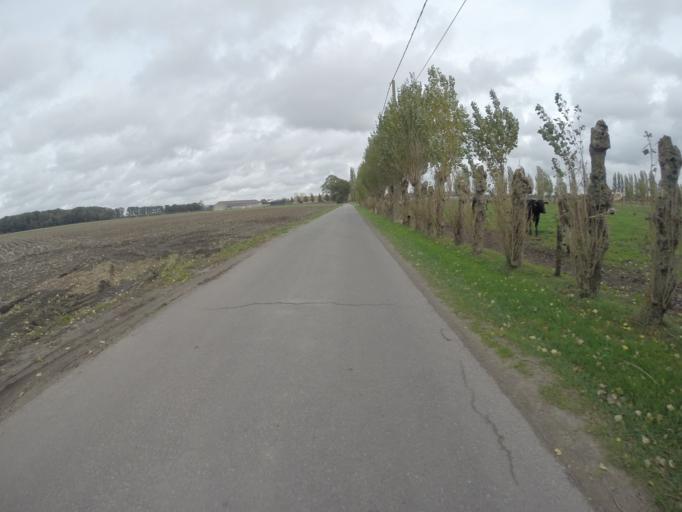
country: BE
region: Flanders
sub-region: Provincie Oost-Vlaanderen
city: Knesselare
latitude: 51.1517
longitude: 3.3975
